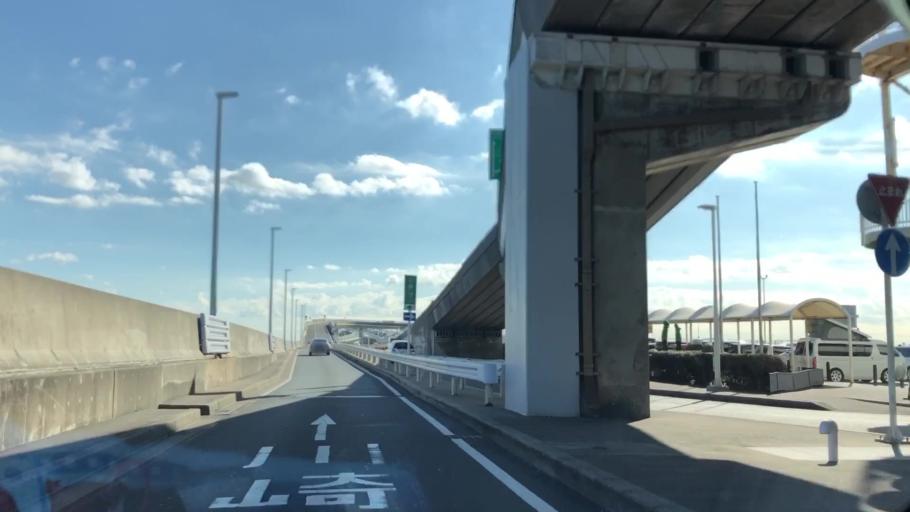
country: JP
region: Chiba
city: Kisarazu
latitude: 35.4643
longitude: 139.8753
